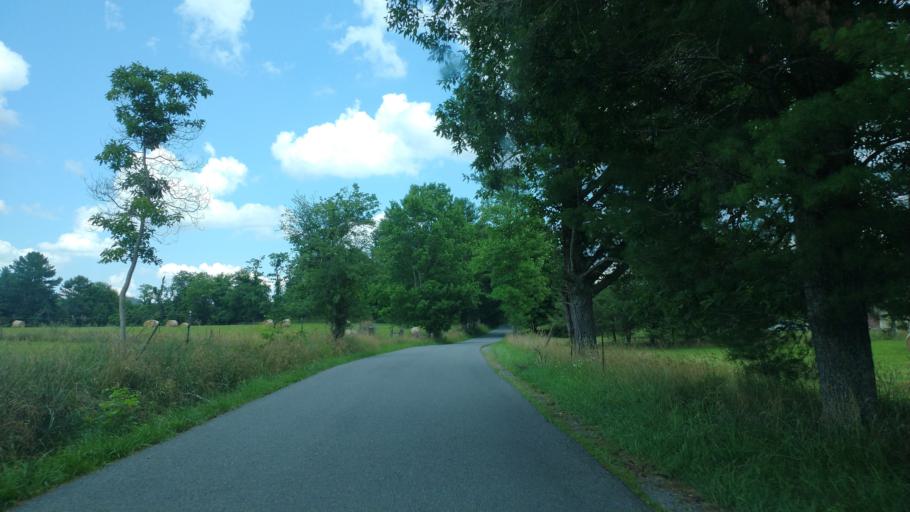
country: US
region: West Virginia
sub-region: Mercer County
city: Athens
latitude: 37.4568
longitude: -81.0336
